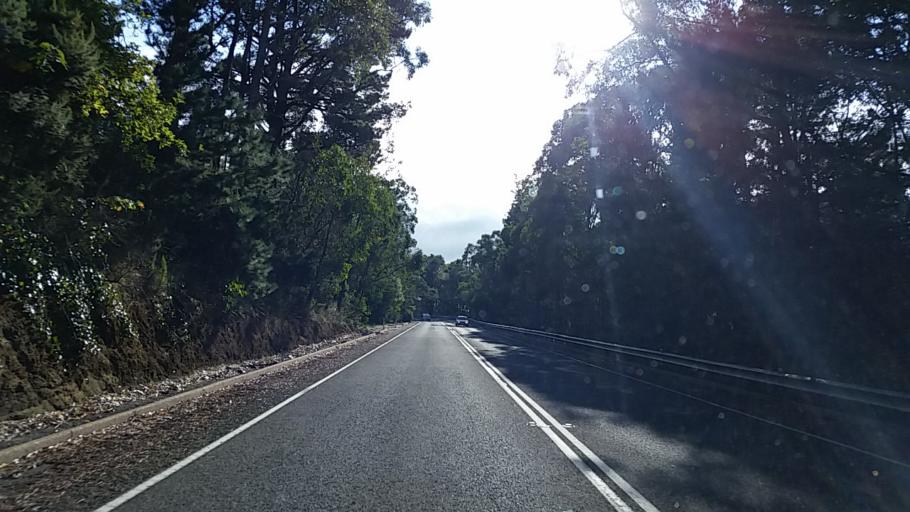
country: AU
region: South Australia
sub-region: Adelaide Hills
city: Crafers
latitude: -34.9939
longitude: 138.7081
